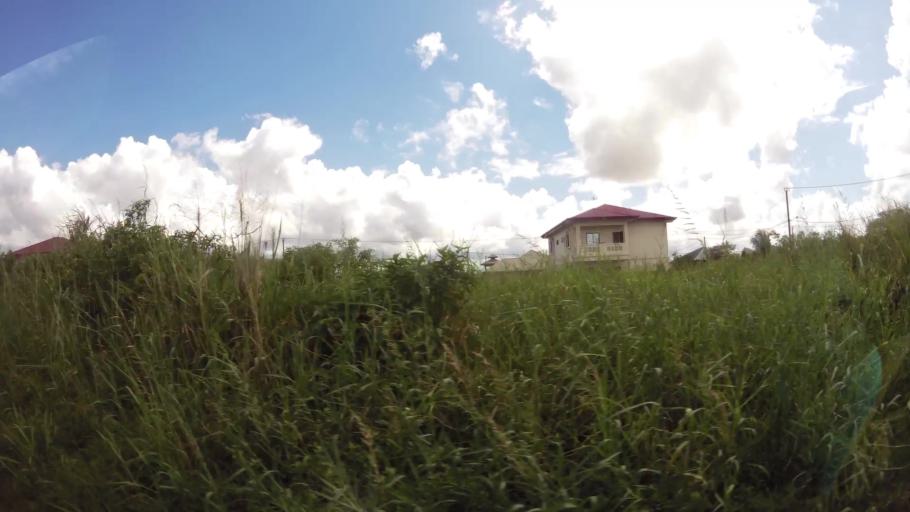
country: SR
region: Paramaribo
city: Paramaribo
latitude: 5.8672
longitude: -55.1323
